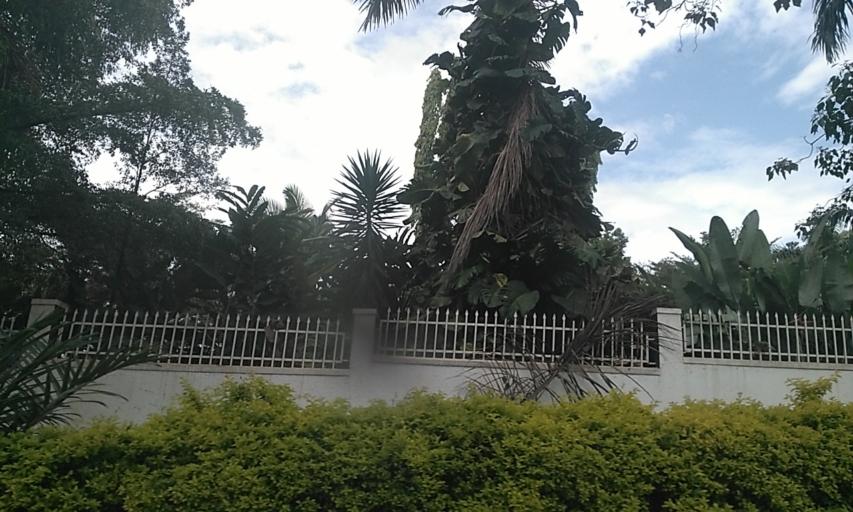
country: UG
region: Central Region
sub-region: Kampala District
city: Kampala
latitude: 0.3219
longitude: 32.5958
